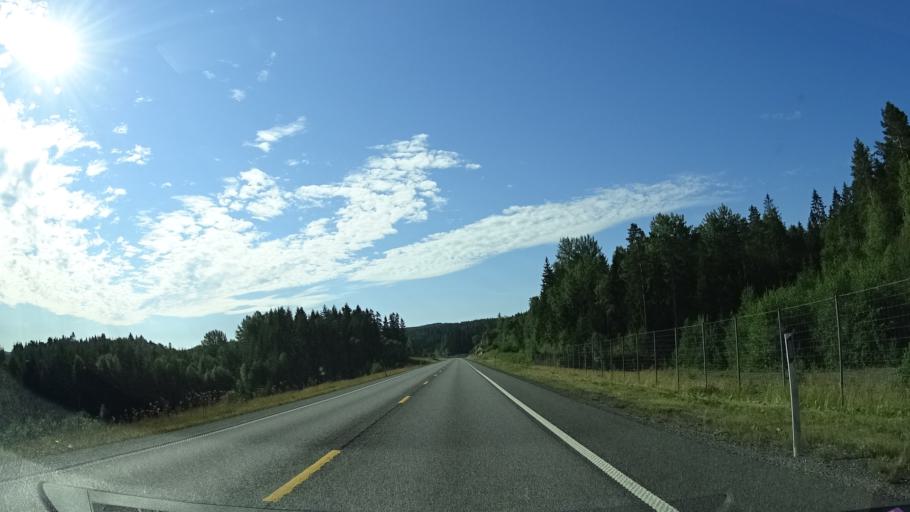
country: NO
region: Ostfold
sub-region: Marker
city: Orje
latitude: 59.5293
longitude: 11.5724
